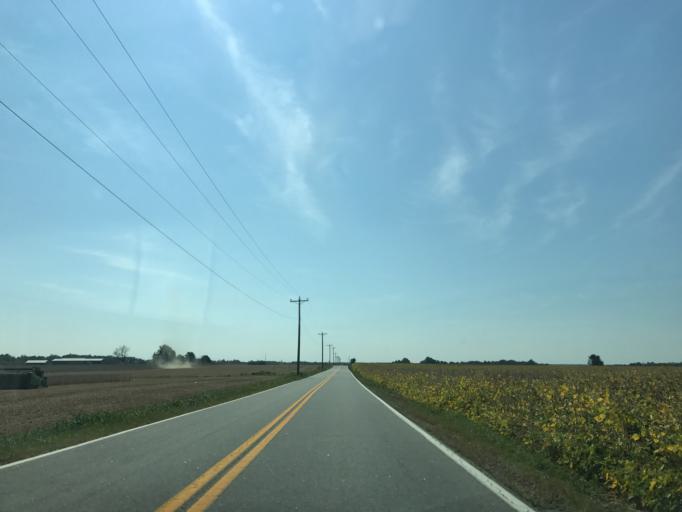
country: US
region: Maryland
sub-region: Queen Anne's County
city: Kingstown
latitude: 39.2732
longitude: -75.9444
